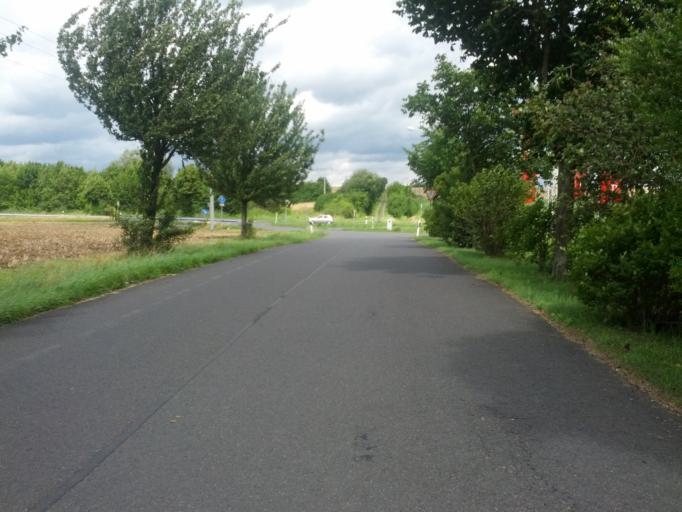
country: DE
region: Thuringia
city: Bischofroda
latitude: 50.9948
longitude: 10.3735
